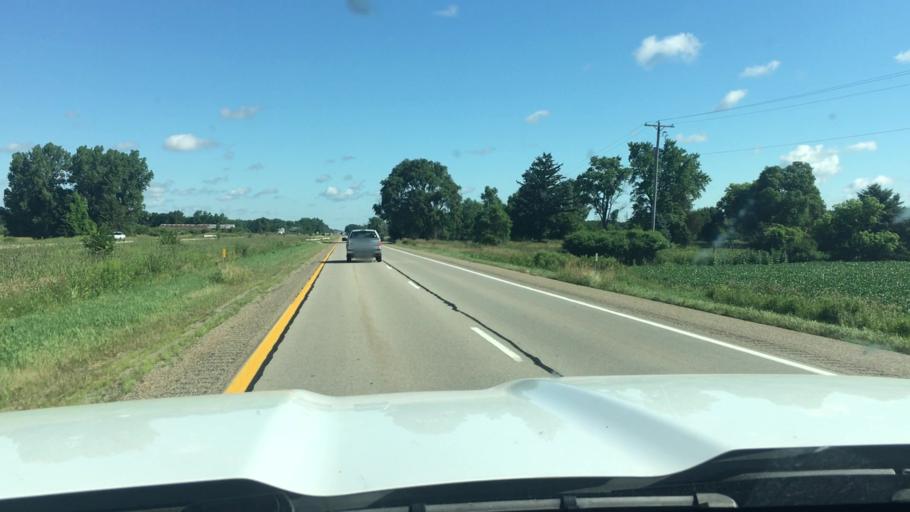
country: US
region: Michigan
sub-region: Clinton County
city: Saint Johns
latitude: 43.1244
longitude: -84.5631
